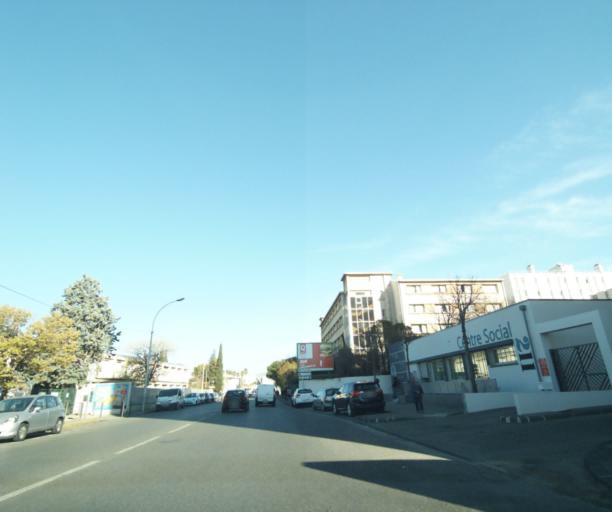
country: FR
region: Provence-Alpes-Cote d'Azur
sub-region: Departement des Bouches-du-Rhone
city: Marseille 10
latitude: 43.2751
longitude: 5.4161
